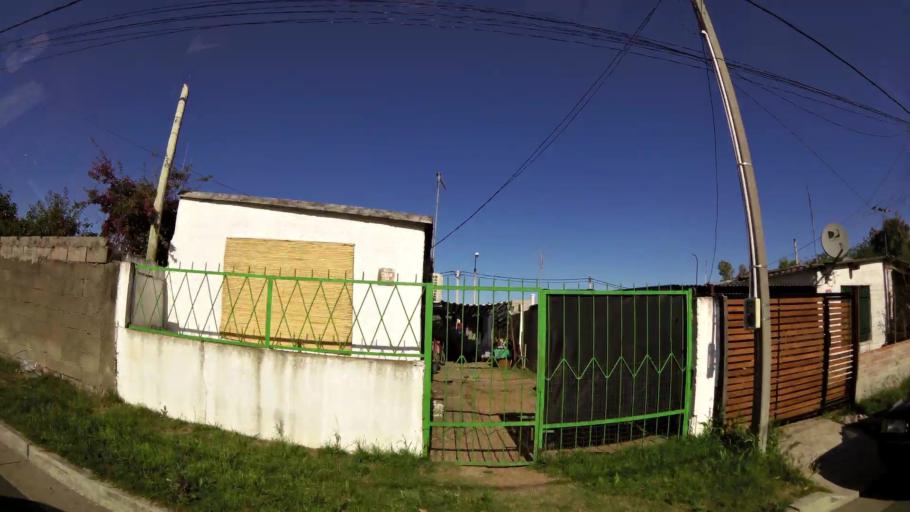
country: UY
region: Canelones
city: La Paz
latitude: -34.8210
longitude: -56.1750
